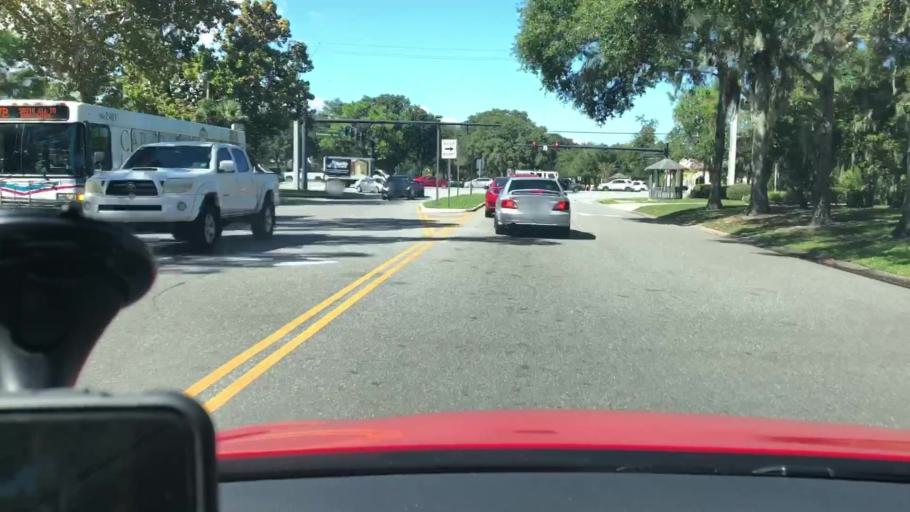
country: US
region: Florida
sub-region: Volusia County
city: Port Orange
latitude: 29.1227
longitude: -81.0115
